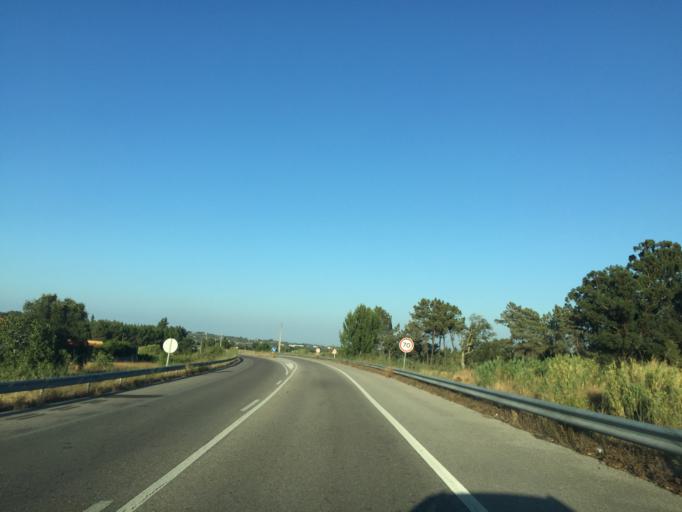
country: PT
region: Santarem
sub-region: Cartaxo
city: Pontevel
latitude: 39.1539
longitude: -8.8685
